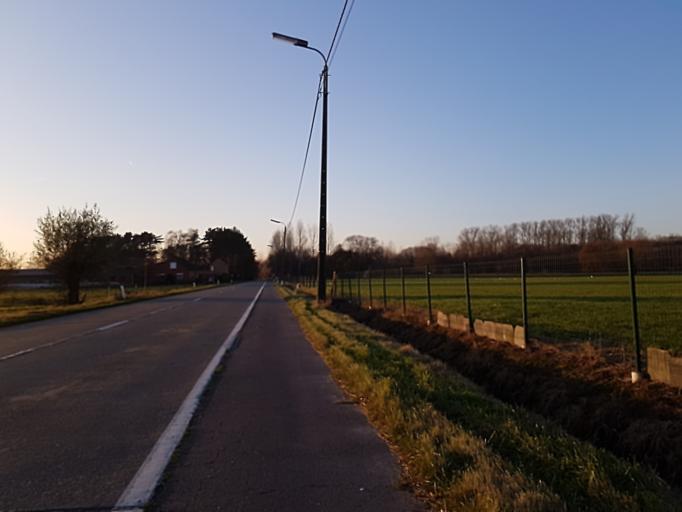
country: BE
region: Flanders
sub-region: Provincie Vlaams-Brabant
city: Boortmeerbeek
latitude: 51.0036
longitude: 4.5705
